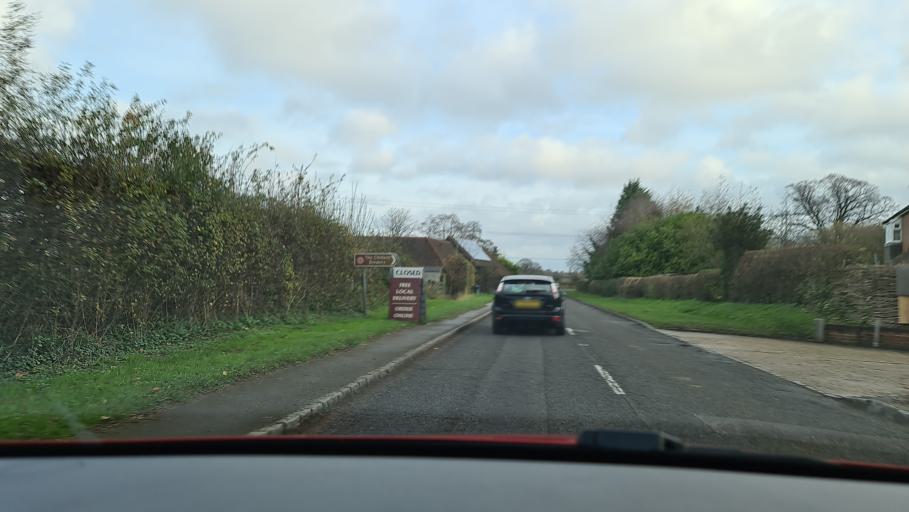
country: GB
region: England
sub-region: Buckinghamshire
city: Weston Turville
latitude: 51.7678
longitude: -0.7810
